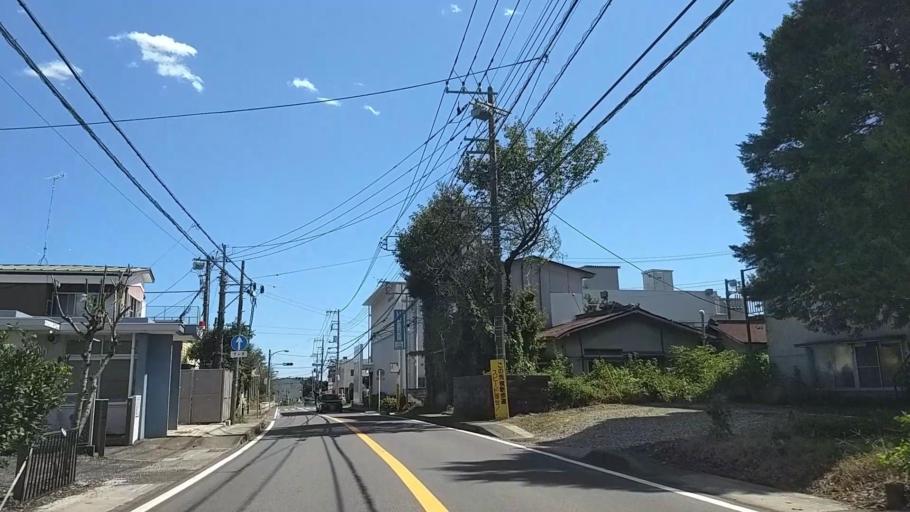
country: JP
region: Kanagawa
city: Zama
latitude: 35.5348
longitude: 139.3111
